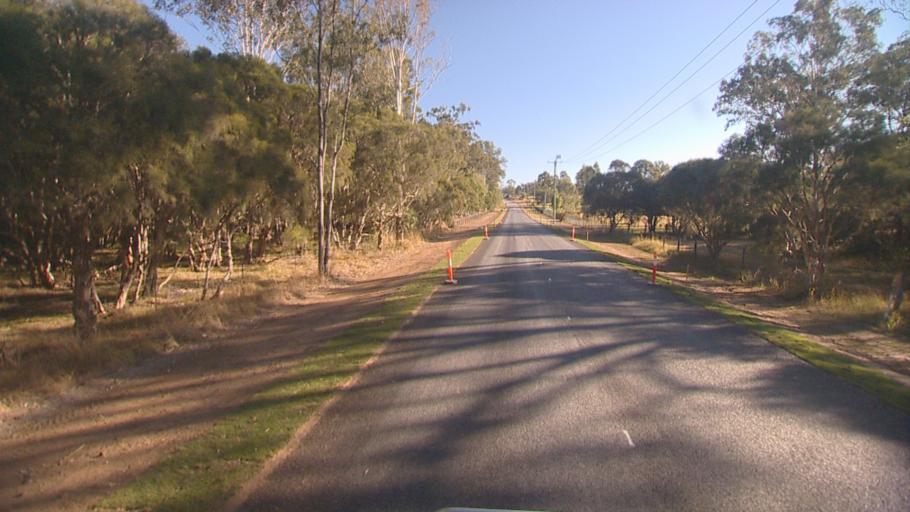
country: AU
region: Queensland
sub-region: Logan
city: Cedar Vale
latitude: -27.8345
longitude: 152.9979
